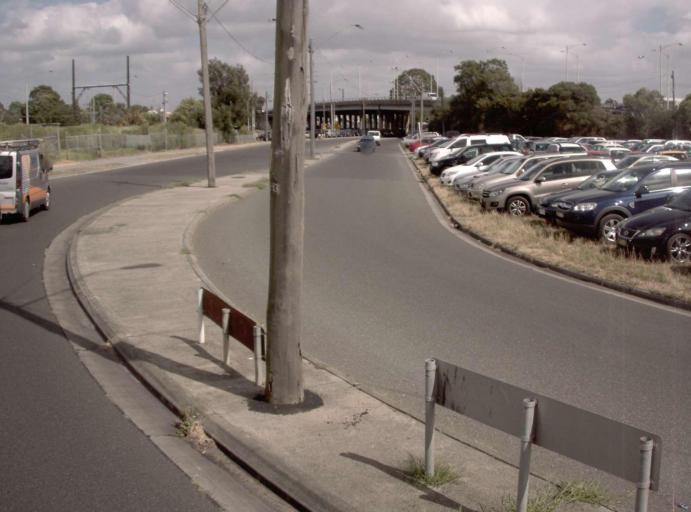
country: AU
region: Victoria
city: Clayton
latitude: -37.9126
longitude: 145.1057
